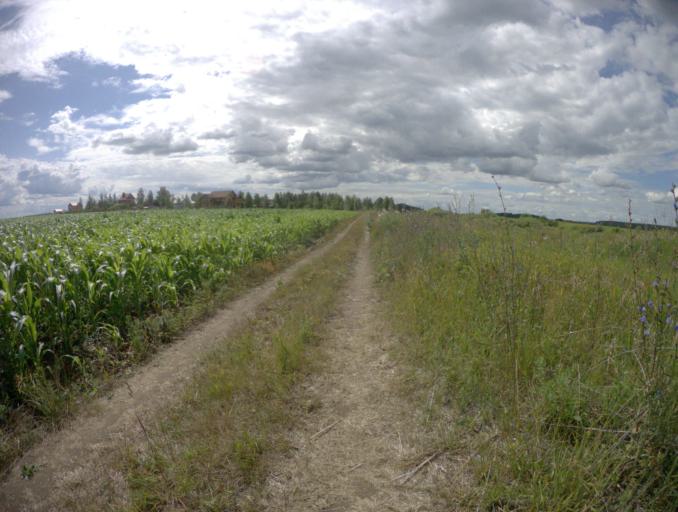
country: RU
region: Vladimir
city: Orgtrud
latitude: 56.3203
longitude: 40.6557
